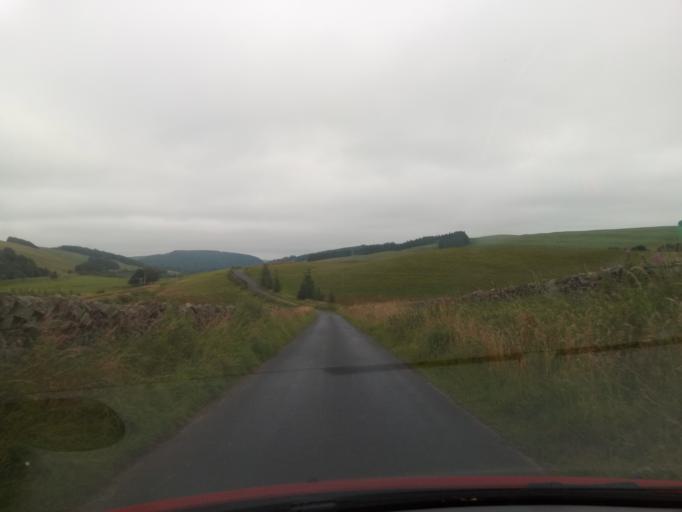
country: GB
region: Scotland
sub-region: Fife
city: Pathhead
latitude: 55.7718
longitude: -2.9459
